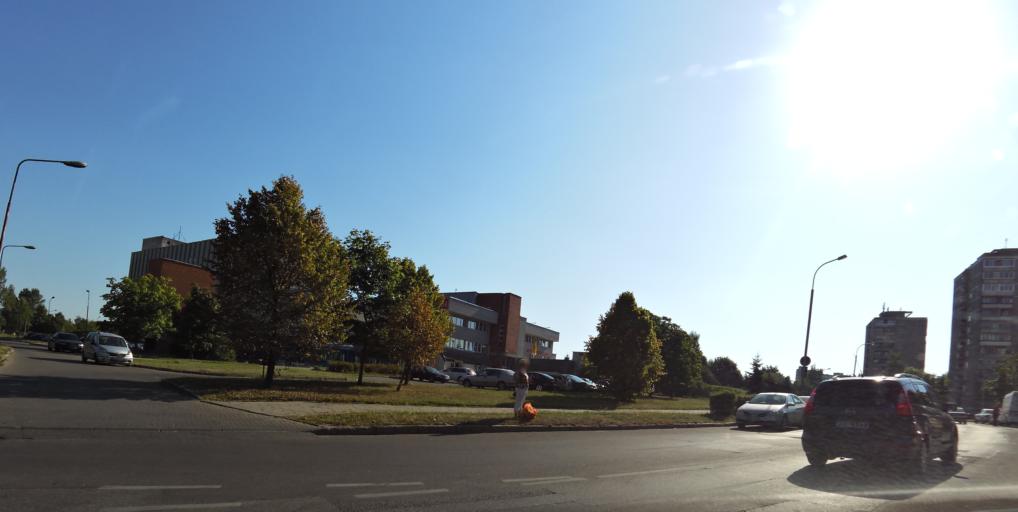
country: LT
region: Vilnius County
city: Justiniskes
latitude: 54.7079
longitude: 25.2224
